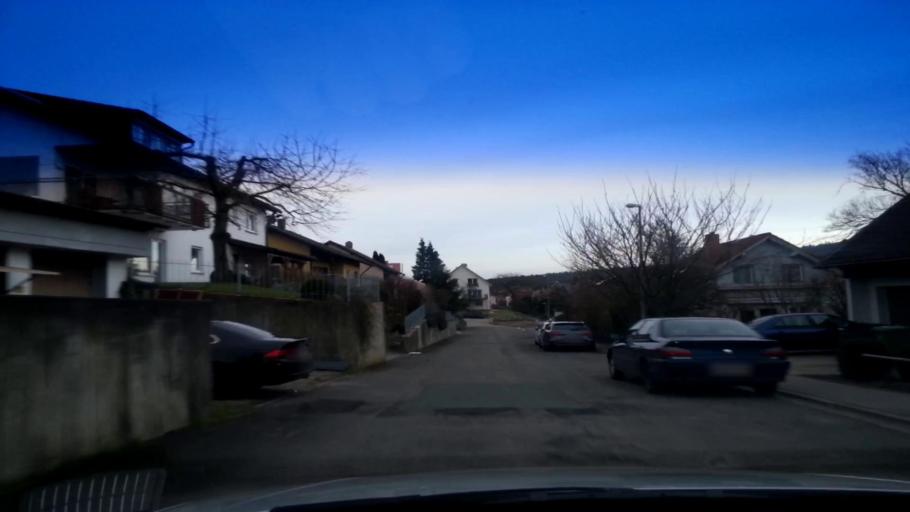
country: DE
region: Bavaria
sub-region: Upper Franconia
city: Litzendorf
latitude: 49.9222
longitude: 11.0029
